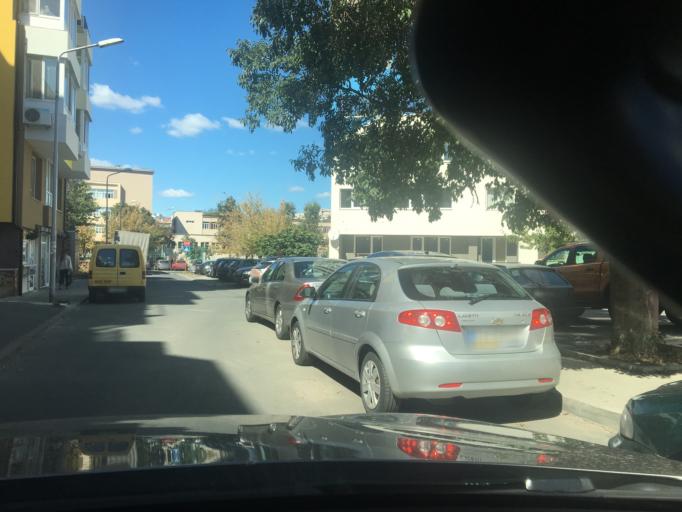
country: BG
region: Burgas
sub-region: Obshtina Burgas
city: Burgas
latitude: 42.5077
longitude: 27.4729
